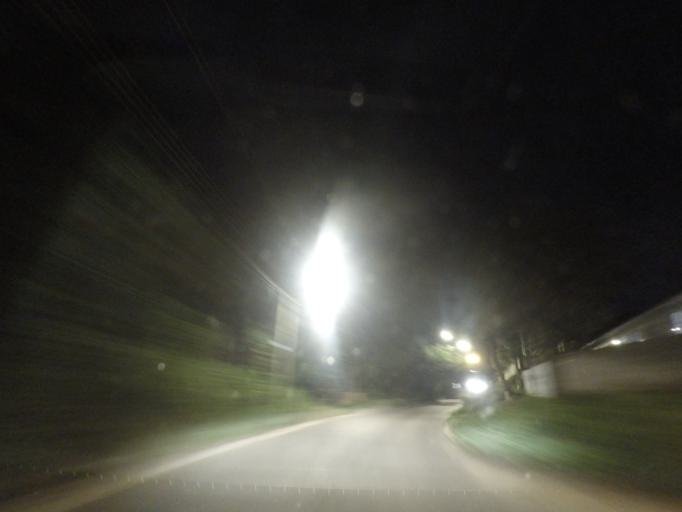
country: BR
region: Parana
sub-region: Almirante Tamandare
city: Almirante Tamandare
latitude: -25.3685
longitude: -49.2819
